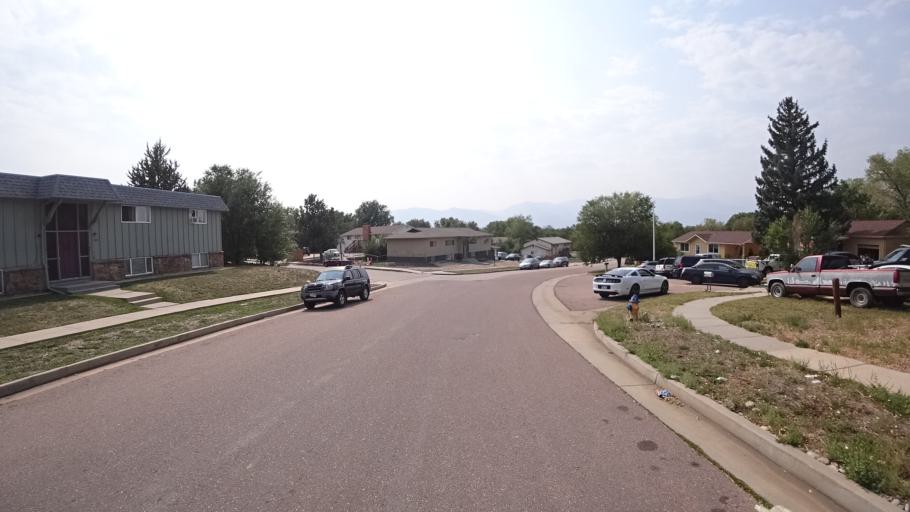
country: US
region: Colorado
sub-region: El Paso County
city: Cimarron Hills
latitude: 38.8270
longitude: -104.7462
